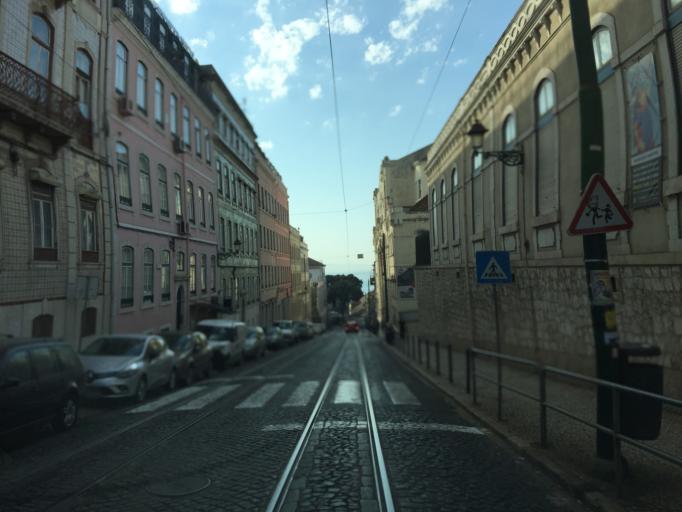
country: PT
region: Lisbon
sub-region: Lisbon
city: Lisbon
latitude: 38.7163
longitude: -9.1294
